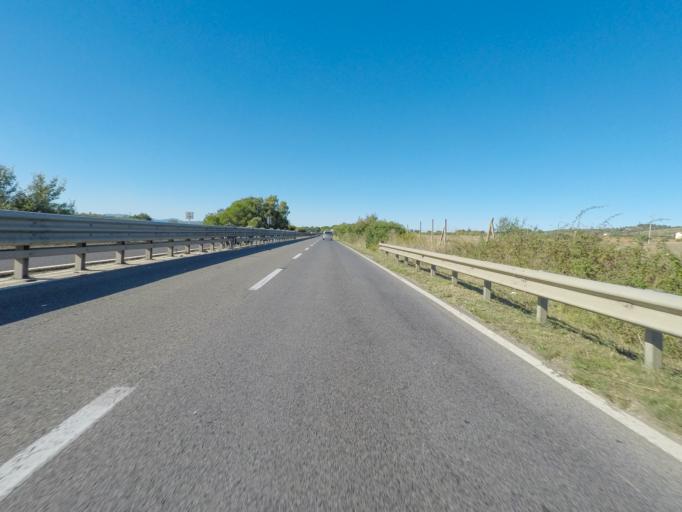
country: IT
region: Tuscany
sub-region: Provincia di Grosseto
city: Grosseto
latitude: 42.7192
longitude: 11.1406
